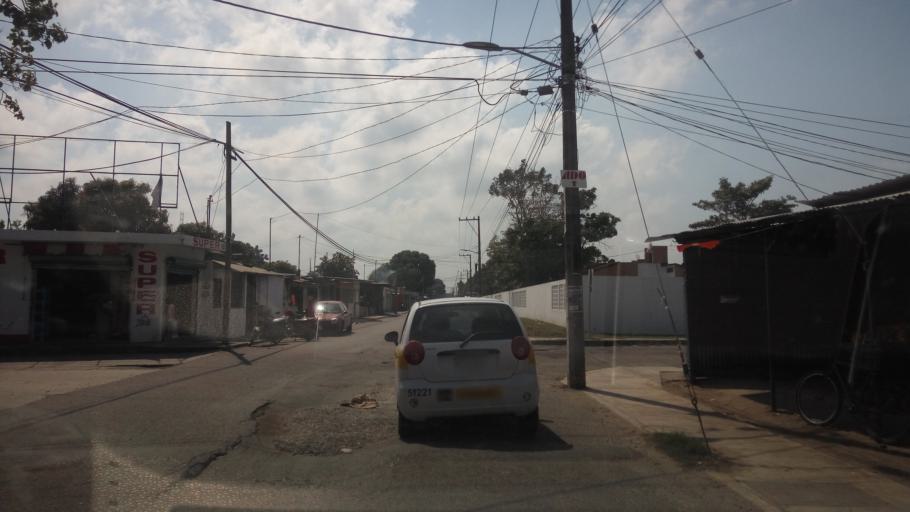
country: MX
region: Tabasco
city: Frontera
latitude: 18.5289
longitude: -92.6401
